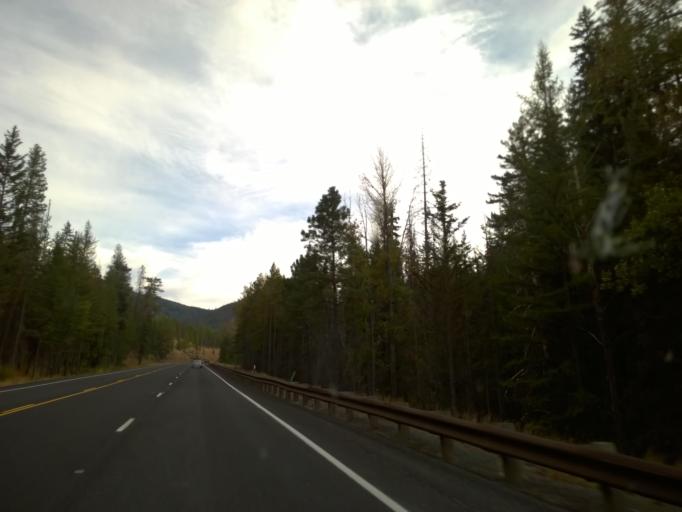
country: US
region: Washington
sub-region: Chelan County
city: Cashmere
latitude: 47.3425
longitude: -120.5658
